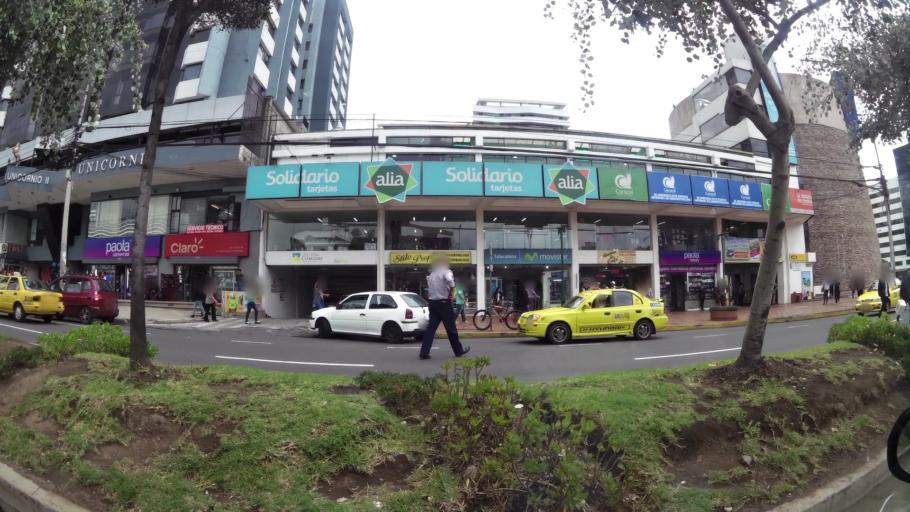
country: EC
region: Pichincha
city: Quito
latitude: -0.1767
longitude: -78.4857
